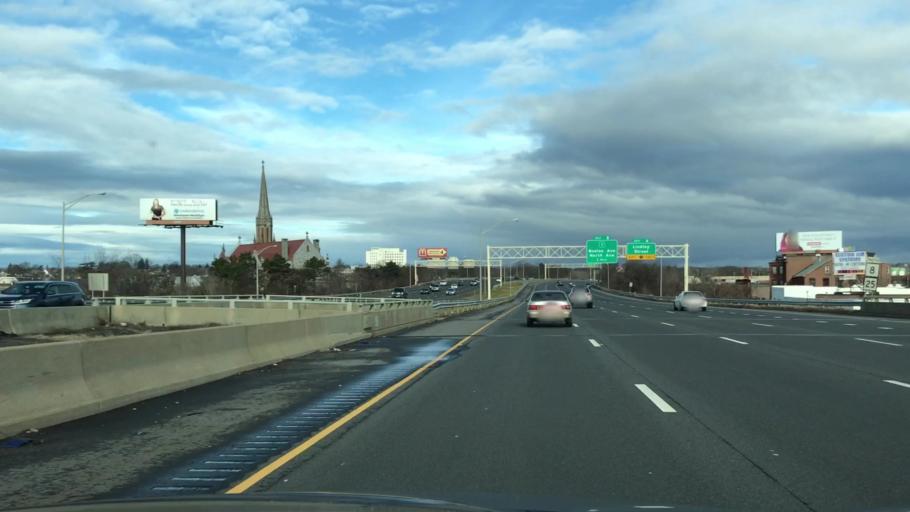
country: US
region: Connecticut
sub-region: Fairfield County
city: Bridgeport
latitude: 41.1903
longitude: -73.1937
